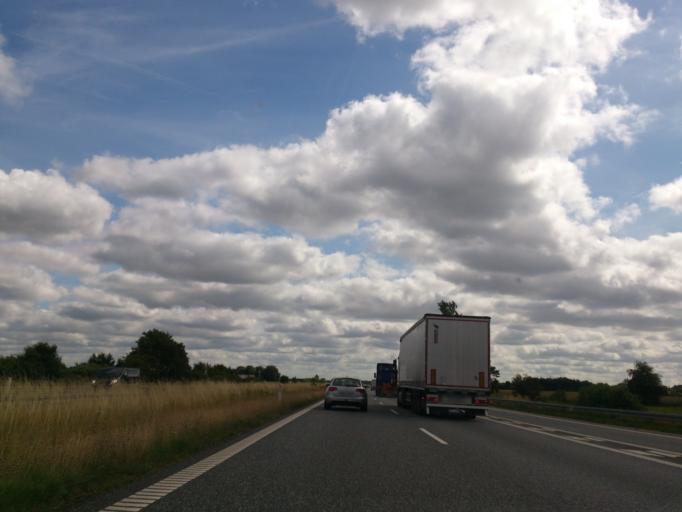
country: DK
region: South Denmark
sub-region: Aabenraa Kommune
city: Krusa
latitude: 54.9122
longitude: 9.3814
